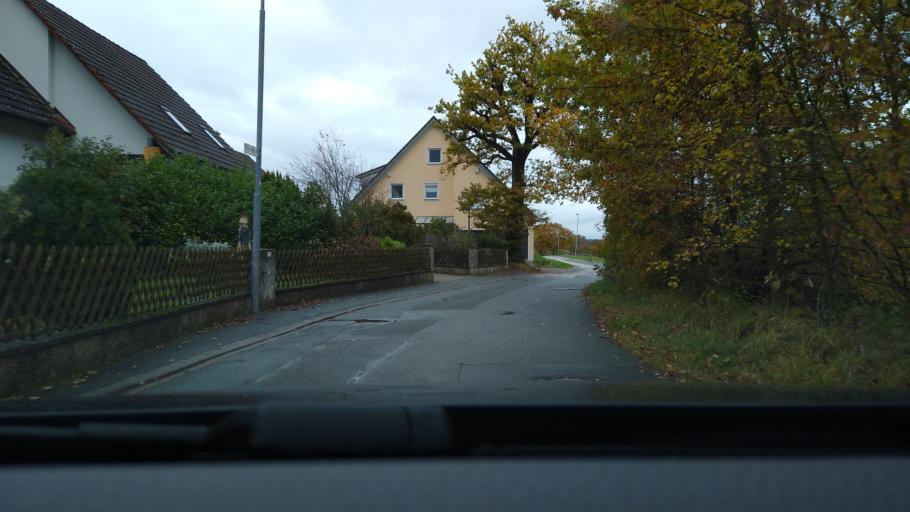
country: DE
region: Bavaria
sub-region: Regierungsbezirk Mittelfranken
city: Hemhofen
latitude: 49.6958
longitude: 10.9292
